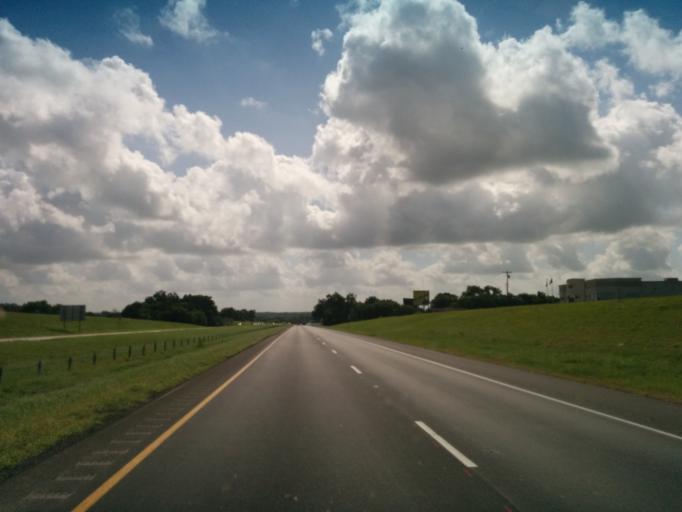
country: US
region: Texas
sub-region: Fayette County
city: Schulenburg
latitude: 29.6948
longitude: -96.8930
